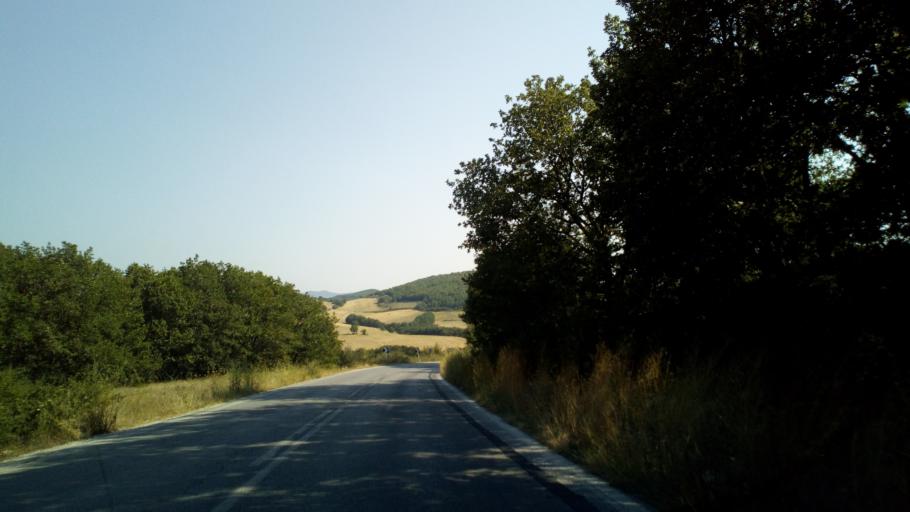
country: GR
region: Central Macedonia
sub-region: Nomos Chalkidikis
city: Polygyros
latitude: 40.4819
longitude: 23.4014
